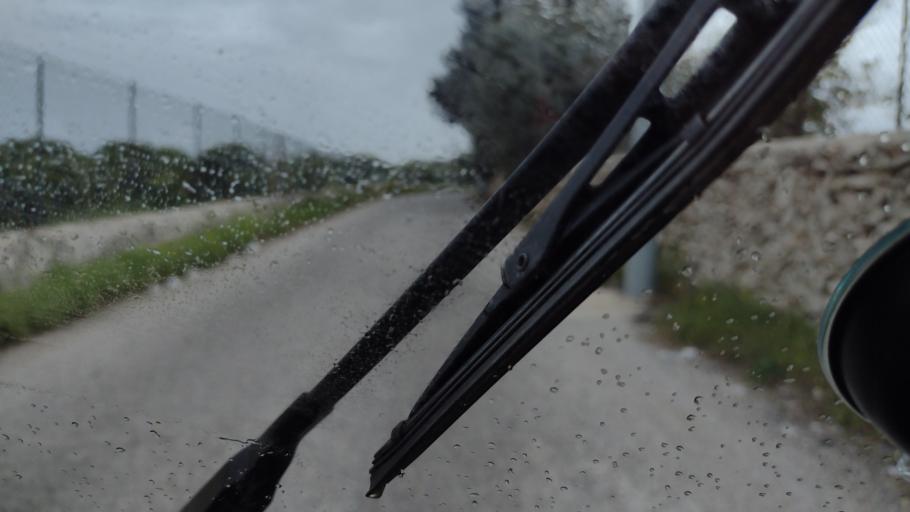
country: IT
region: Sicily
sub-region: Provincia di Siracusa
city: Avola
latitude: 36.8854
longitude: 15.1280
